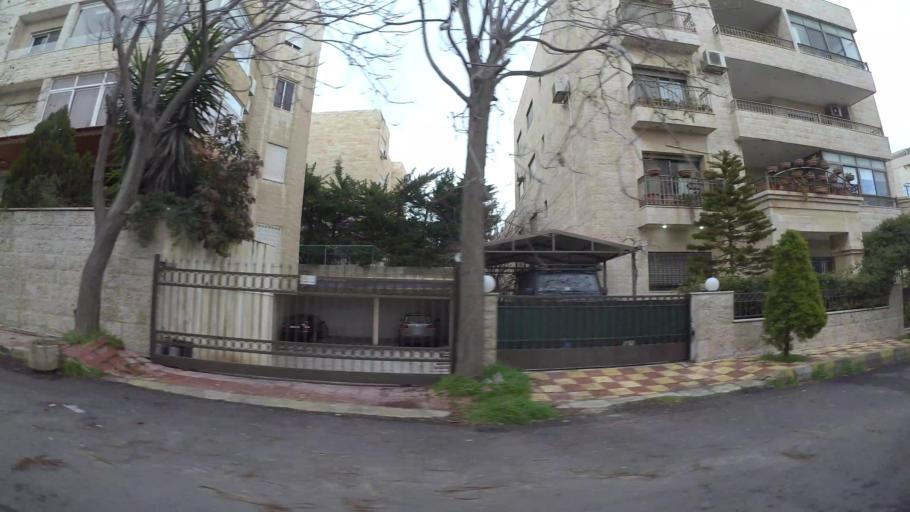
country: JO
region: Amman
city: Wadi as Sir
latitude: 31.9508
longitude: 35.8745
